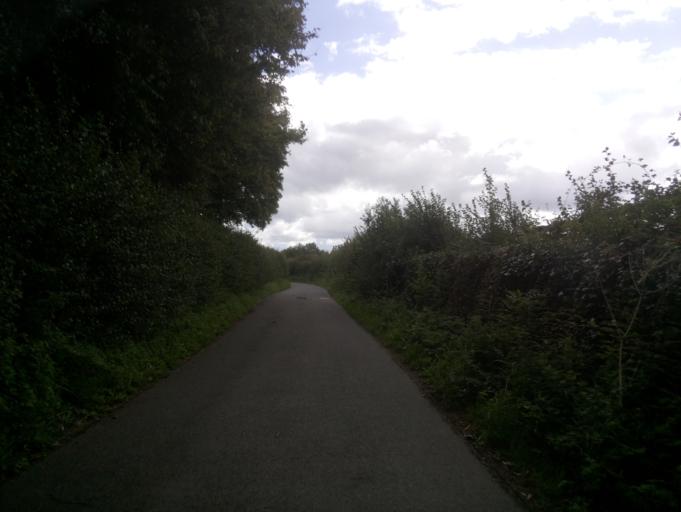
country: GB
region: England
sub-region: Wiltshire
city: Nettleton
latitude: 51.5023
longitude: -2.2650
